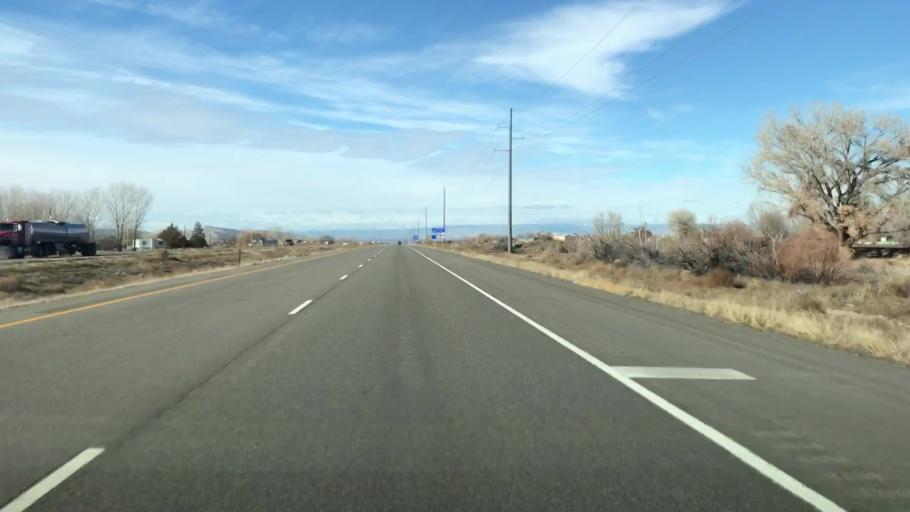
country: US
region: Colorado
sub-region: Mesa County
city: Fruita
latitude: 39.1402
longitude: -108.7058
